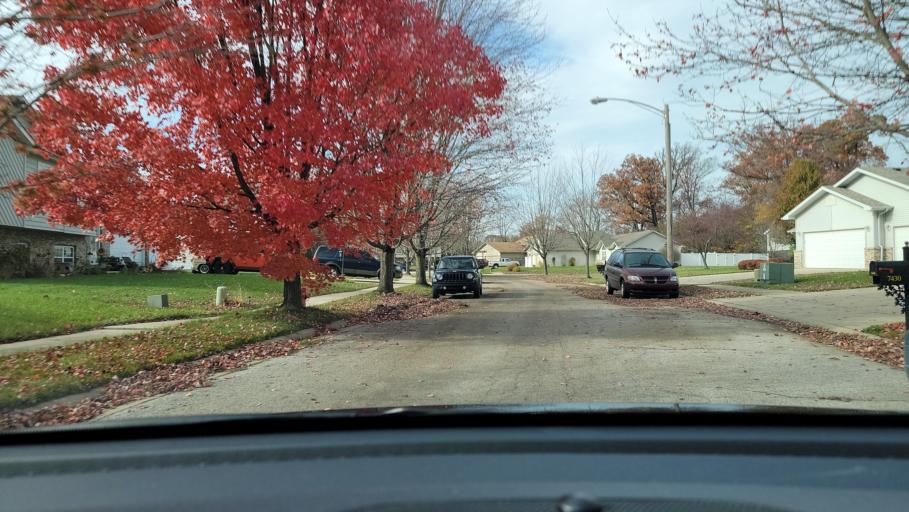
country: US
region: Indiana
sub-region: Porter County
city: Burns Harbor
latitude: 41.5838
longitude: -87.1275
